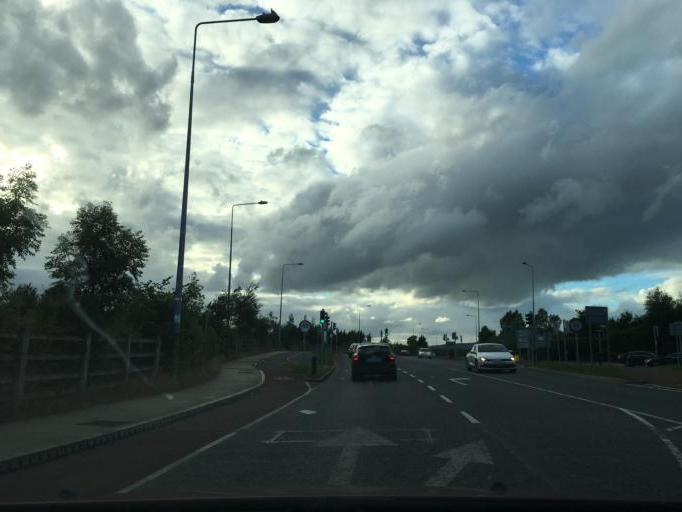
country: IE
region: Leinster
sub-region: Wicklow
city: Rathnew
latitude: 52.9887
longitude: -6.0664
